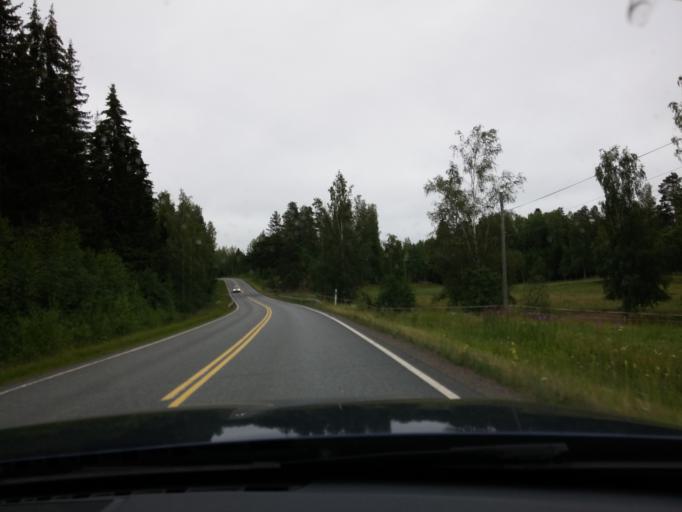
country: FI
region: Central Finland
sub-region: Joutsa
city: Joutsa
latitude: 61.8013
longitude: 25.9913
